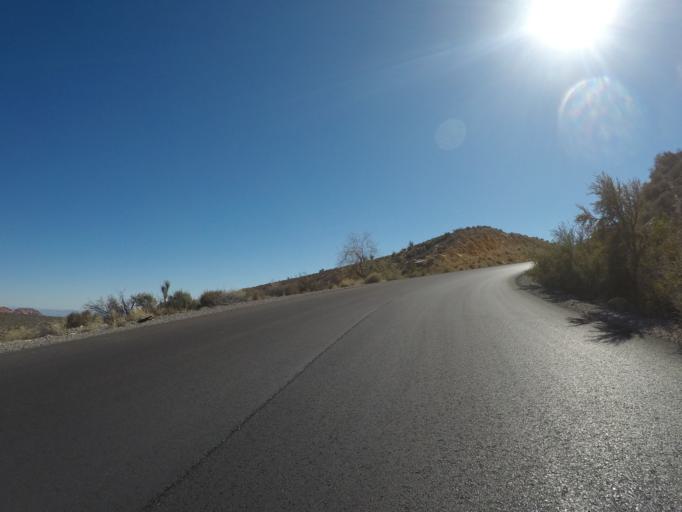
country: US
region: Nevada
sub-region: Clark County
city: Summerlin South
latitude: 36.1565
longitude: -115.4837
